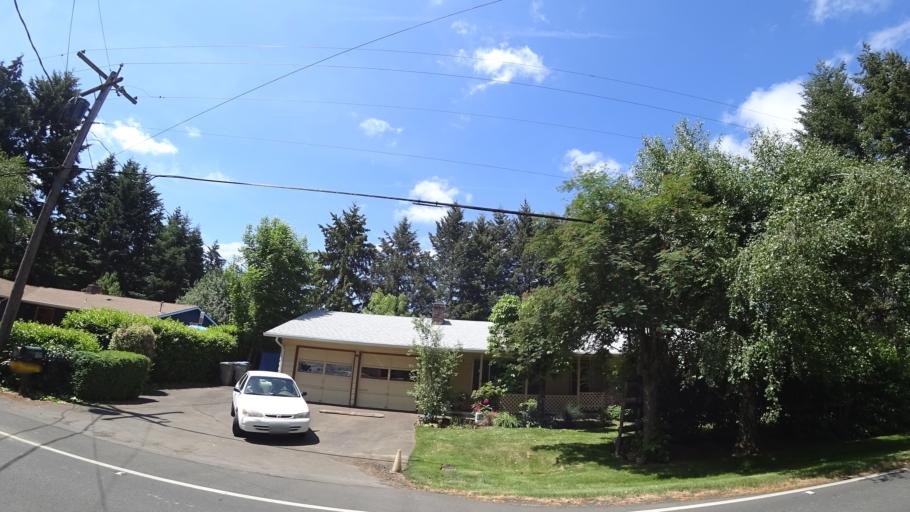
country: US
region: Oregon
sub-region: Washington County
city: King City
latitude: 45.4276
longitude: -122.7999
